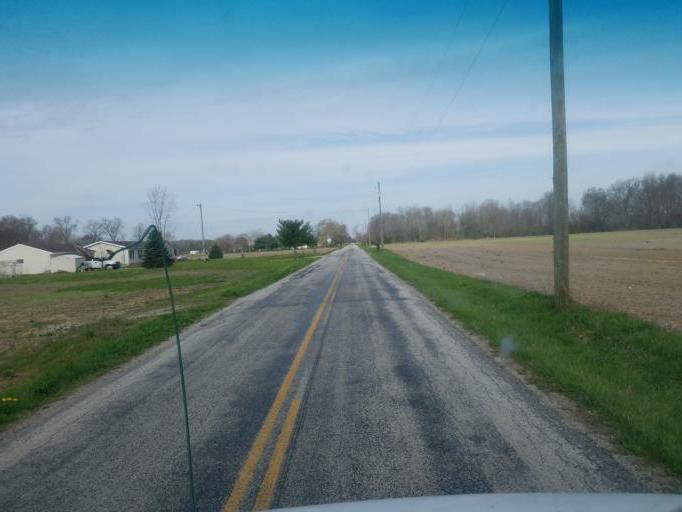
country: US
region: Ohio
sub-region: Marion County
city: Prospect
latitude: 40.4510
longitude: -83.2221
